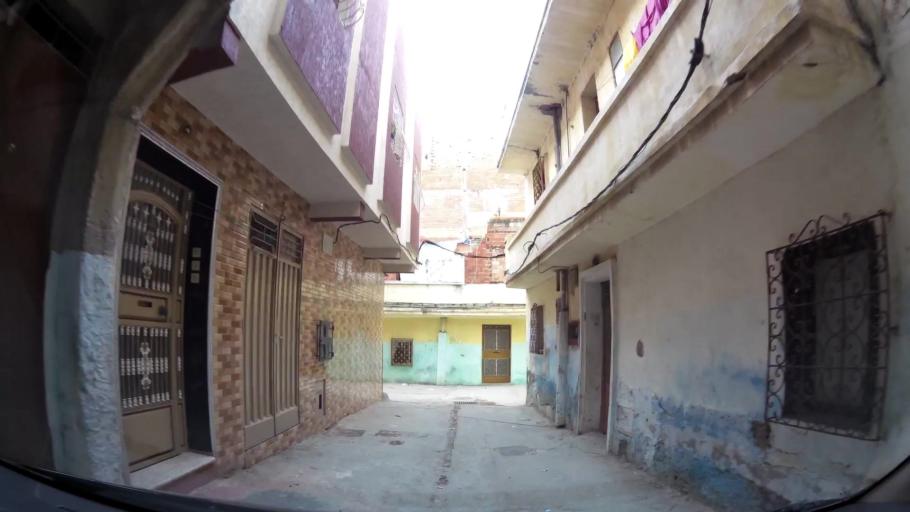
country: MA
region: Tanger-Tetouan
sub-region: Tanger-Assilah
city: Tangier
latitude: 35.7599
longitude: -5.7854
